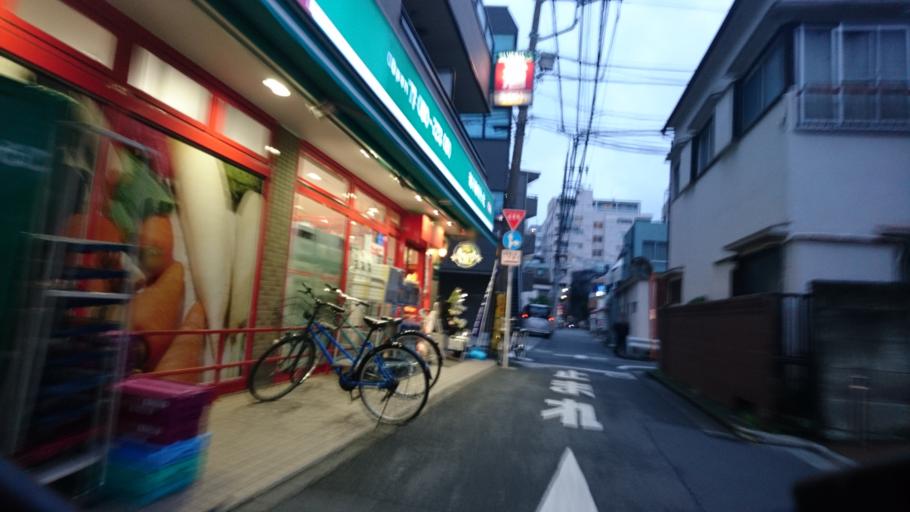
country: JP
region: Kanagawa
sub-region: Kawasaki-shi
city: Kawasaki
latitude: 35.5838
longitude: 139.7257
